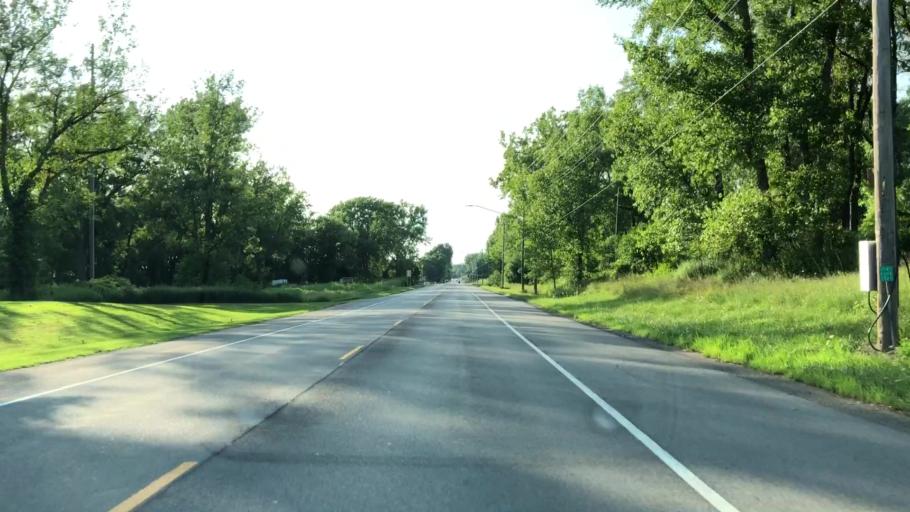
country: US
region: New York
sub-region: Erie County
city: West Seneca
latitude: 42.8597
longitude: -78.7641
